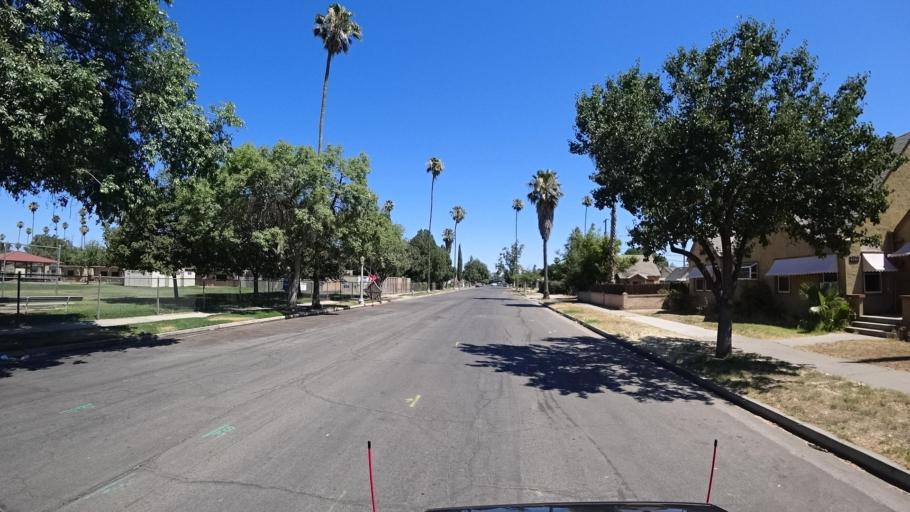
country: US
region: California
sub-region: Fresno County
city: Fresno
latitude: 36.7408
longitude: -119.7611
